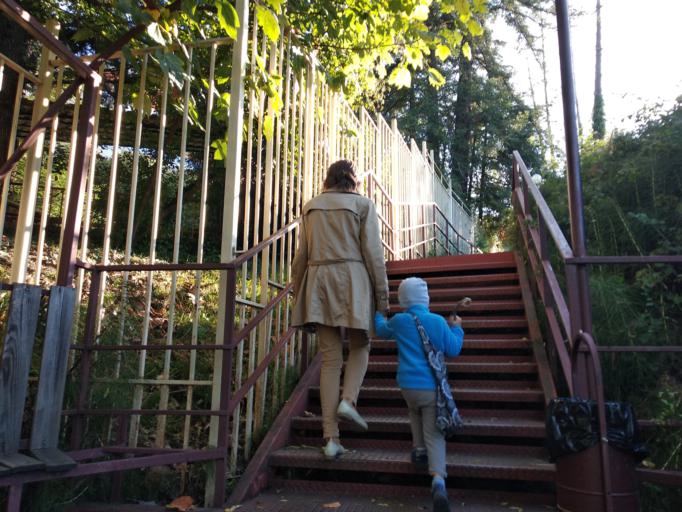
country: RU
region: Krasnodarskiy
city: Gornoye Loo
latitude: 43.6689
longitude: 39.6108
